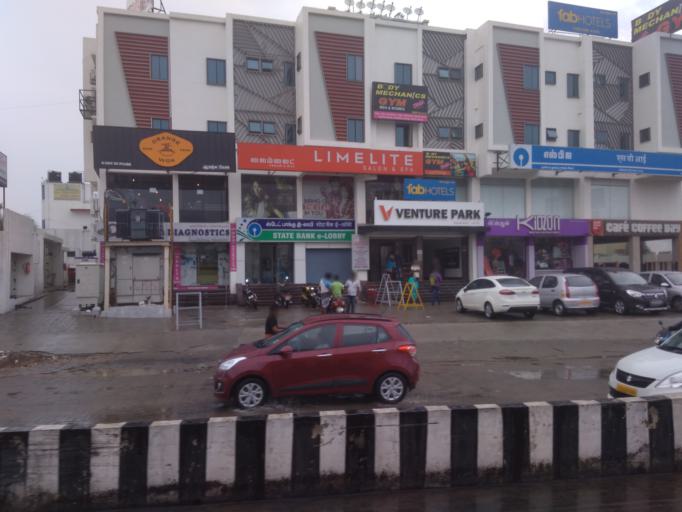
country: IN
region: Tamil Nadu
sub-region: Kancheepuram
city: Injambakkam
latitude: 12.9342
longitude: 80.2329
